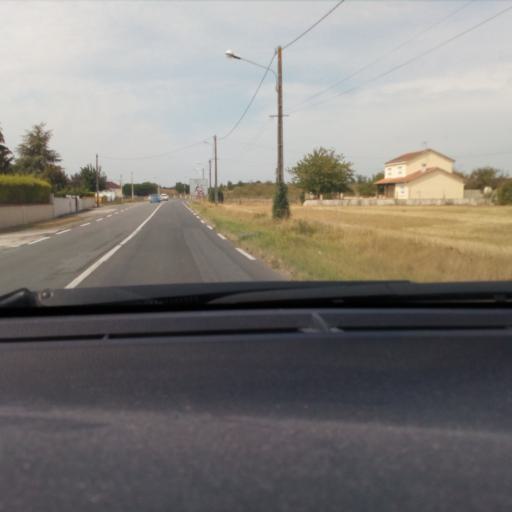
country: FR
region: Poitou-Charentes
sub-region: Departement de la Charente
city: Saint-Yrieix-sur-Charente
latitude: 45.6863
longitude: 0.1099
